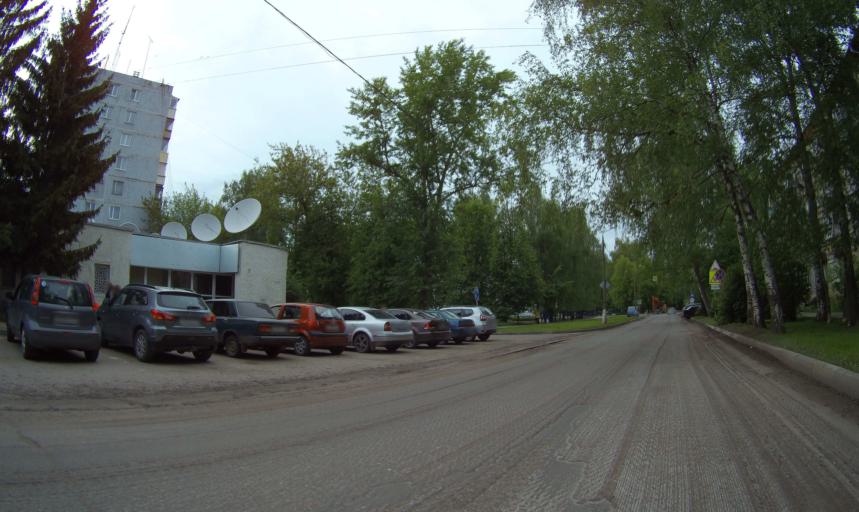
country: RU
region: Moskovskaya
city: Kolomna
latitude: 55.0899
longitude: 38.7628
